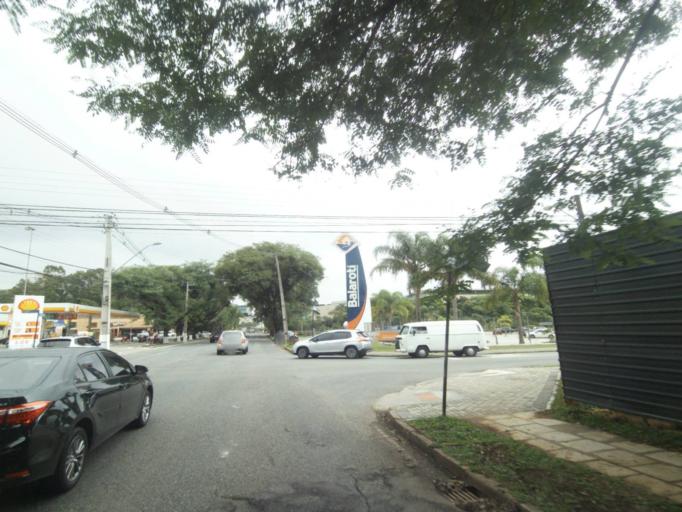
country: BR
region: Parana
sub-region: Curitiba
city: Curitiba
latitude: -25.4368
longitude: -49.3137
